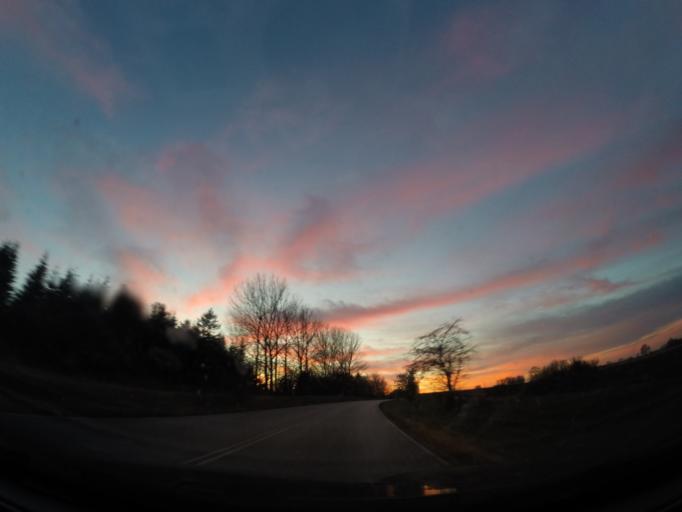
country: DK
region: Capital Region
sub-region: Hoje-Taastrup Kommune
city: Taastrup
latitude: 55.6734
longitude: 12.3057
